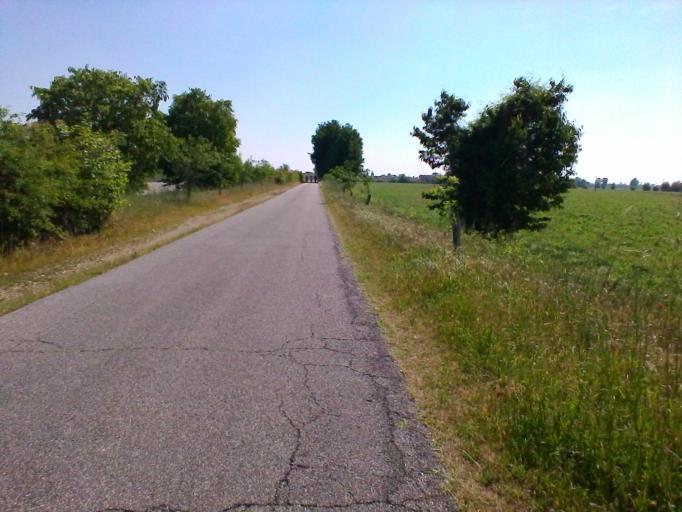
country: IT
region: Lombardy
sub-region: Provincia di Mantova
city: Soave
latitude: 45.1890
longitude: 10.7354
